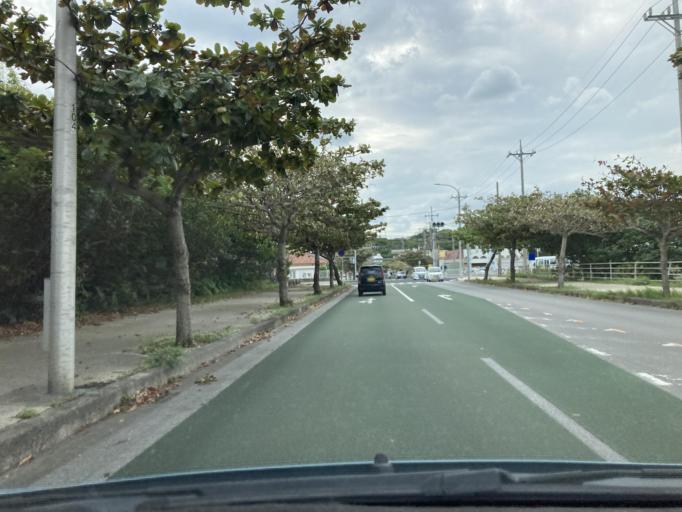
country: JP
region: Okinawa
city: Katsuren-haebaru
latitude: 26.3301
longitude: 127.9040
